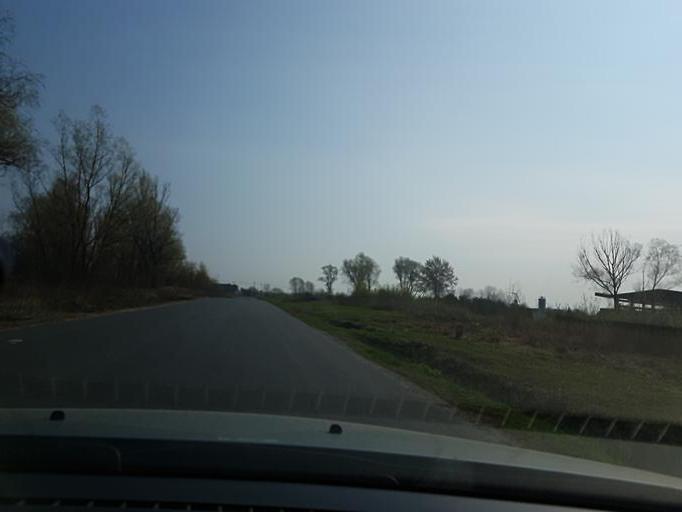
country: PL
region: Lodz Voivodeship
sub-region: Powiat kutnowski
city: Kutno
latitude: 52.2075
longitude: 19.4084
